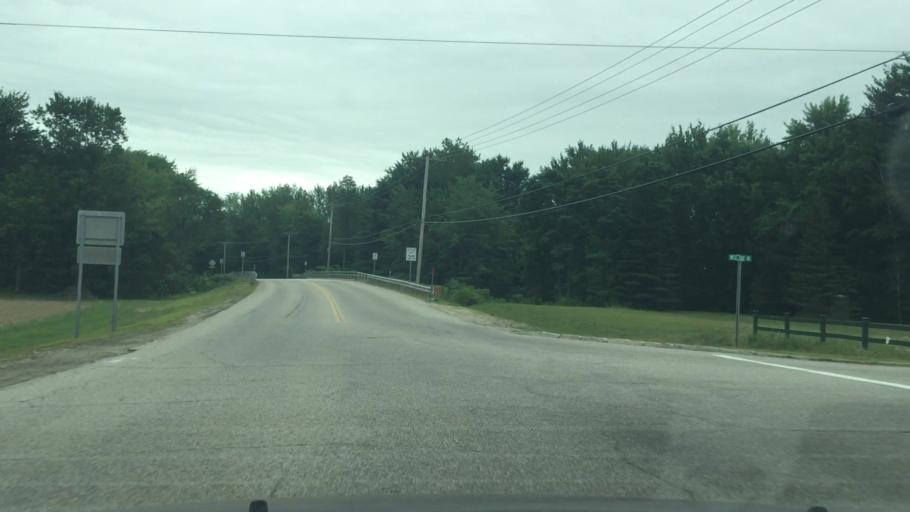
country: US
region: New Hampshire
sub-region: Carroll County
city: North Conway
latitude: 44.0579
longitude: -71.1484
